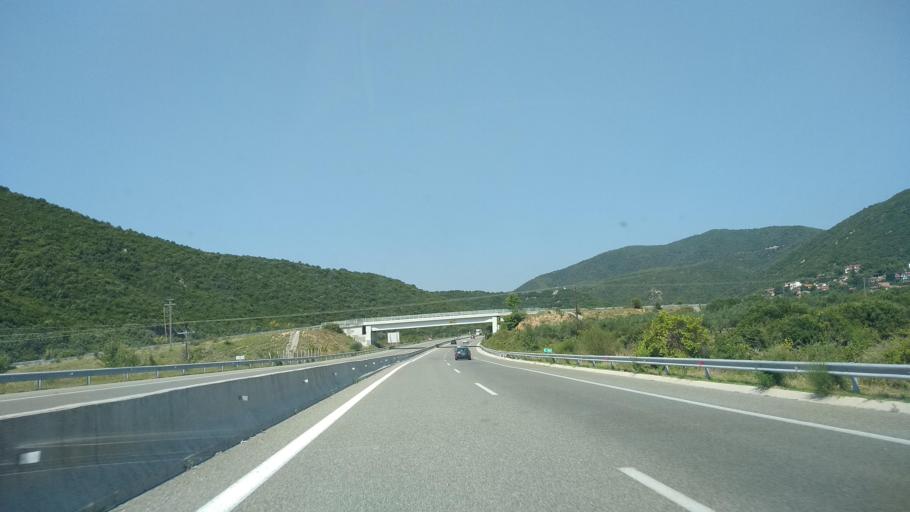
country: GR
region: Central Macedonia
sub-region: Nomos Thessalonikis
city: Nea Vrasna
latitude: 40.7008
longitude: 23.6623
